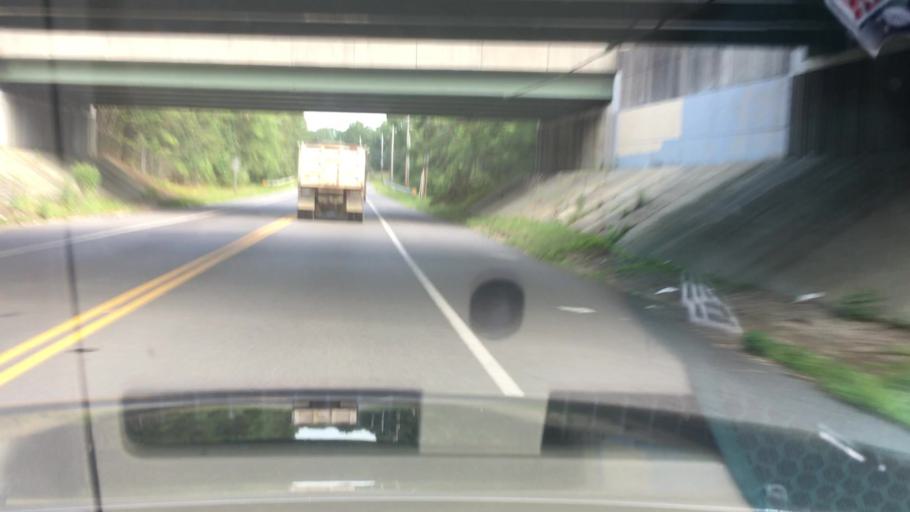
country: US
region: New Jersey
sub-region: Ocean County
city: Vista Center
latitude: 40.1576
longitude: -74.4071
